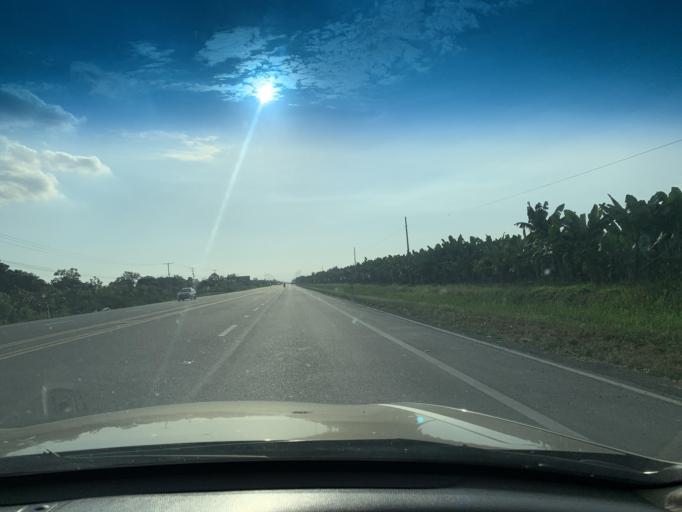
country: EC
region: Guayas
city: Naranjito
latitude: -2.2575
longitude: -79.5744
